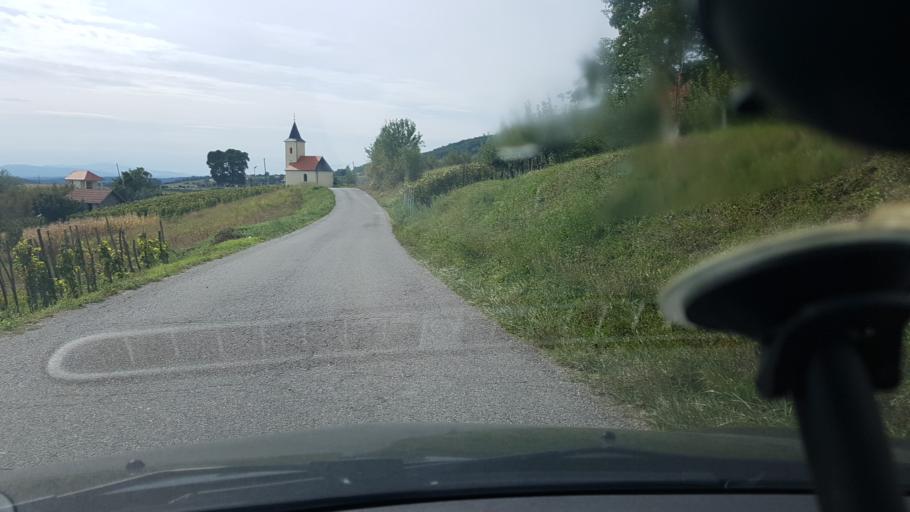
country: HR
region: Varazdinska
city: Ljubescica
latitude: 46.1208
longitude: 16.4300
